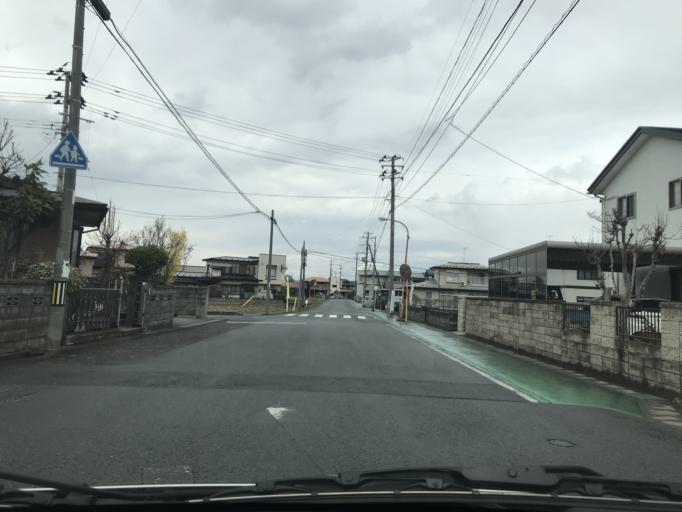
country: JP
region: Iwate
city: Mizusawa
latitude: 39.1465
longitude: 141.1359
